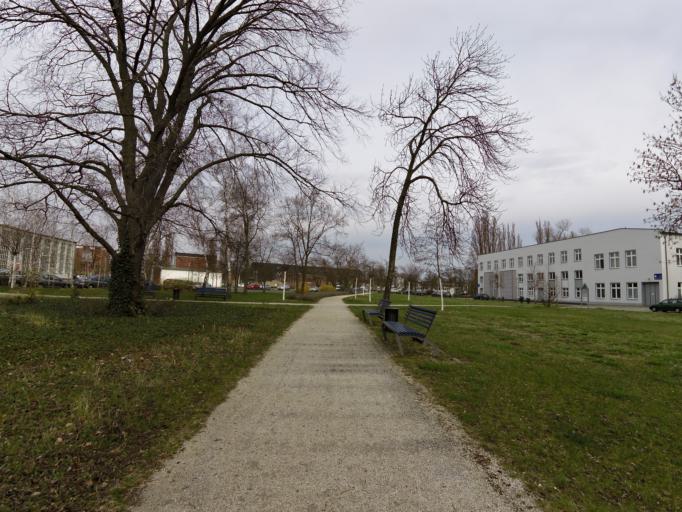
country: DE
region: Berlin
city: Altglienicke
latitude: 52.4300
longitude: 13.5267
